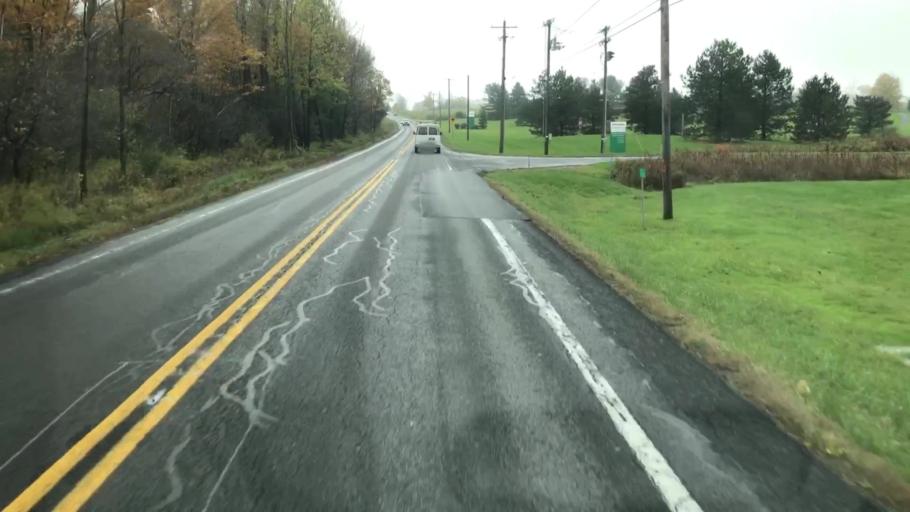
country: US
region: New York
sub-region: Onondaga County
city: Skaneateles
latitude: 42.9790
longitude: -76.4280
